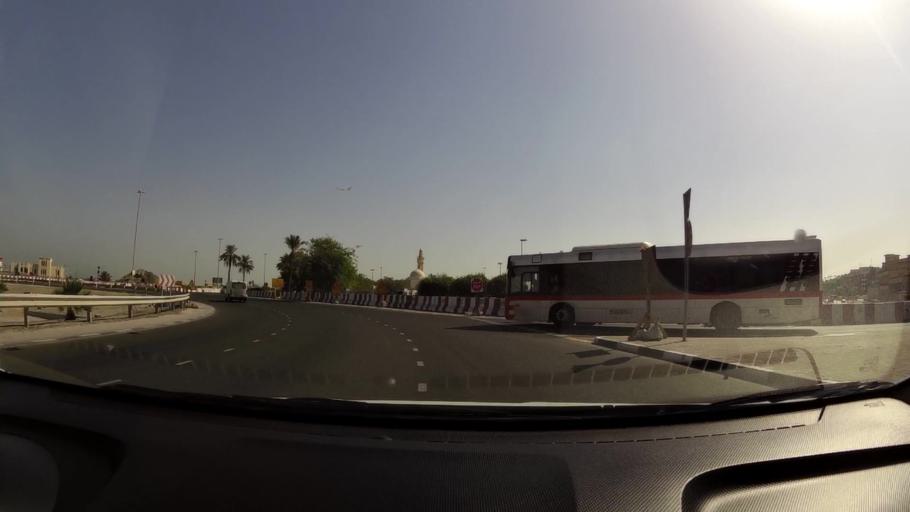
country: AE
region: Ash Shariqah
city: Sharjah
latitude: 25.2737
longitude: 55.2972
